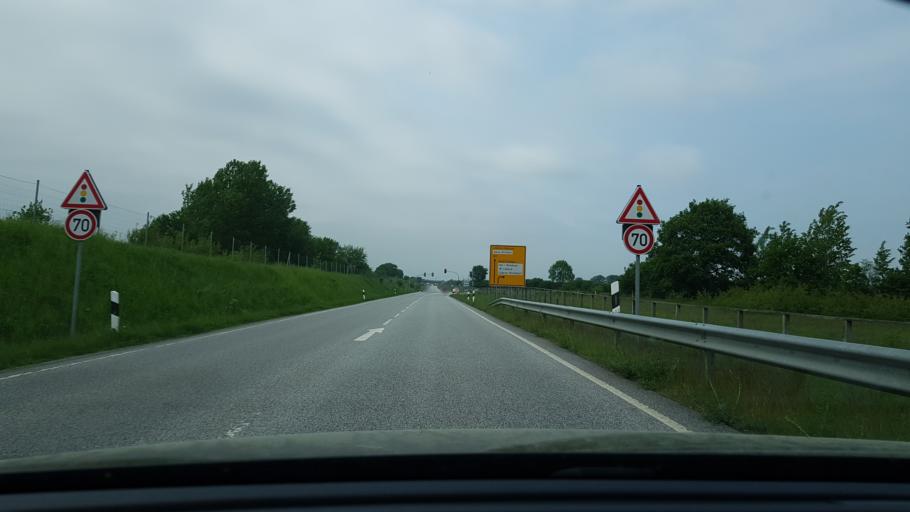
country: DE
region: Schleswig-Holstein
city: Klempau
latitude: 53.8055
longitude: 10.6974
